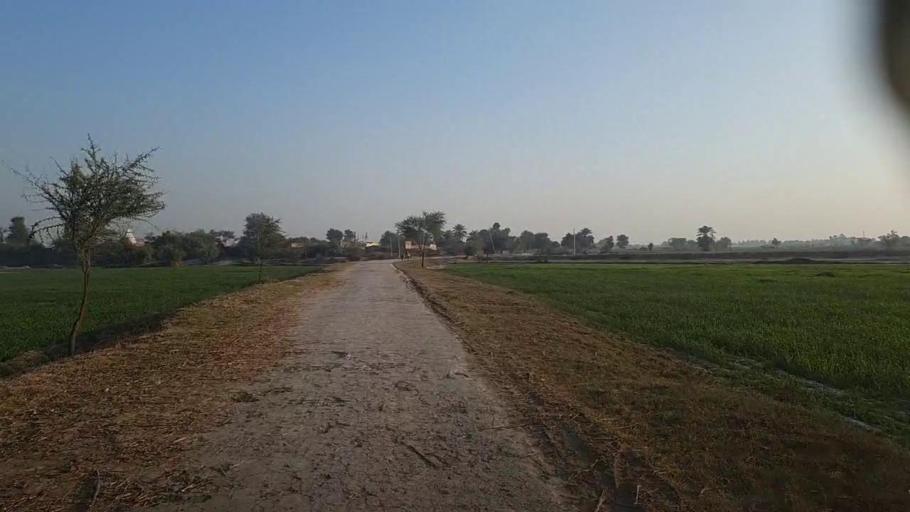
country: PK
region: Sindh
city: Khairpur
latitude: 28.0700
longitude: 69.7503
